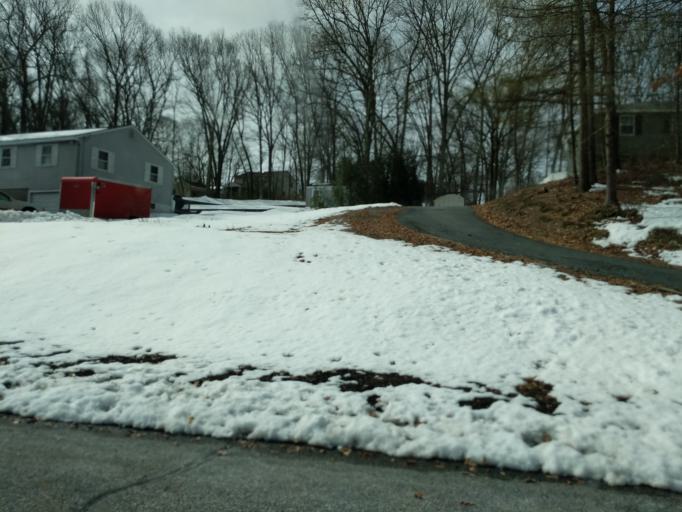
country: US
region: Massachusetts
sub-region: Worcester County
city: Whitinsville
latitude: 42.1084
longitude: -71.6901
